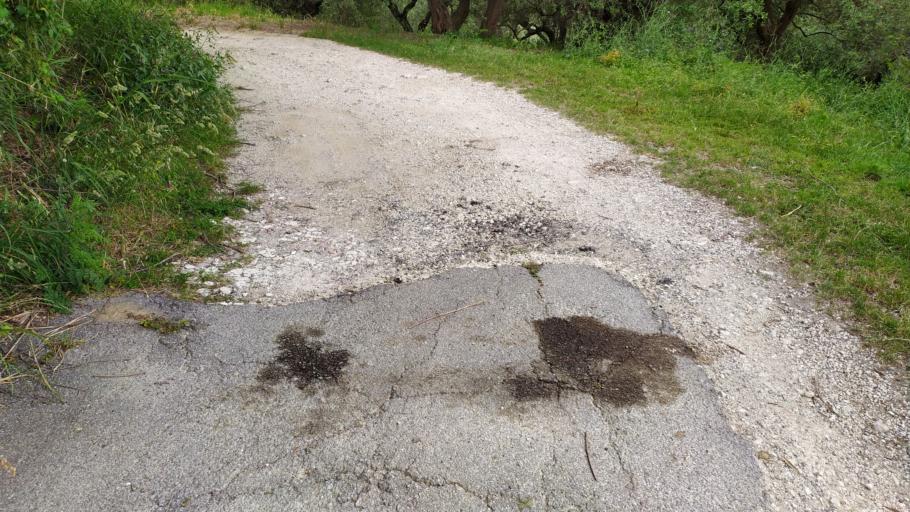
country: IT
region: Sicily
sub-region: Messina
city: Gualtieri Sicamino
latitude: 38.1573
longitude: 15.3008
